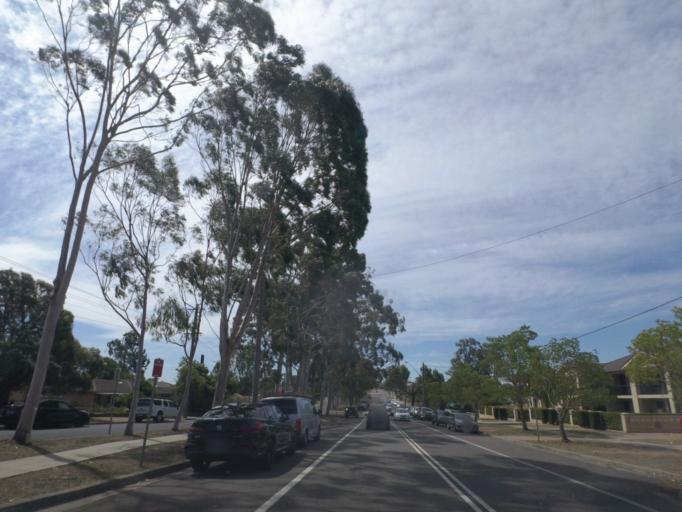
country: AU
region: New South Wales
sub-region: Camden
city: Camden South
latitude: -34.0707
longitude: 150.6943
